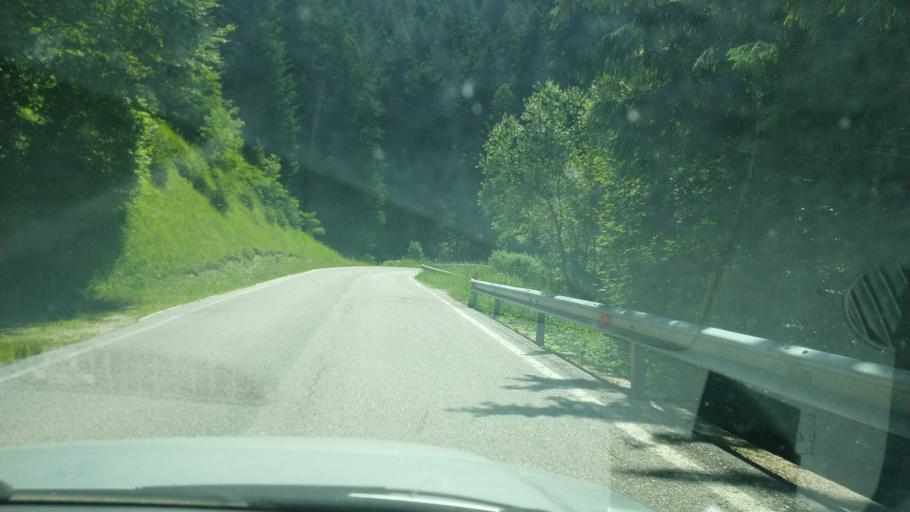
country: IT
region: Trentino-Alto Adige
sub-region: Provincia di Trento
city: Folgaria
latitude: 45.9021
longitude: 11.2122
